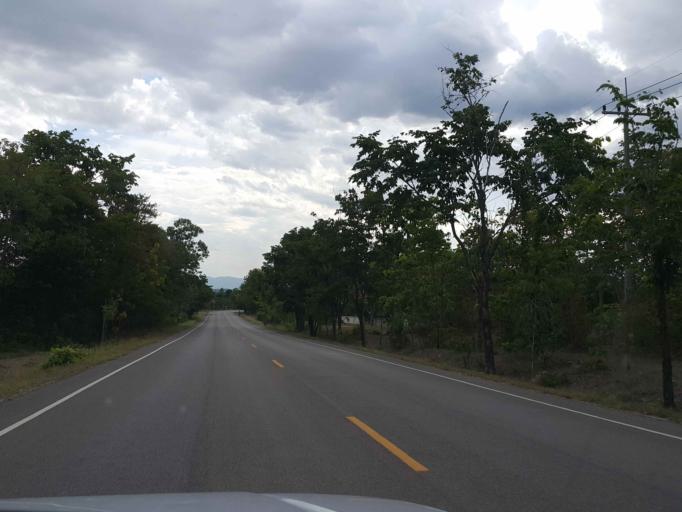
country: TH
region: Lampang
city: Thoen
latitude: 17.6499
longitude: 99.2845
